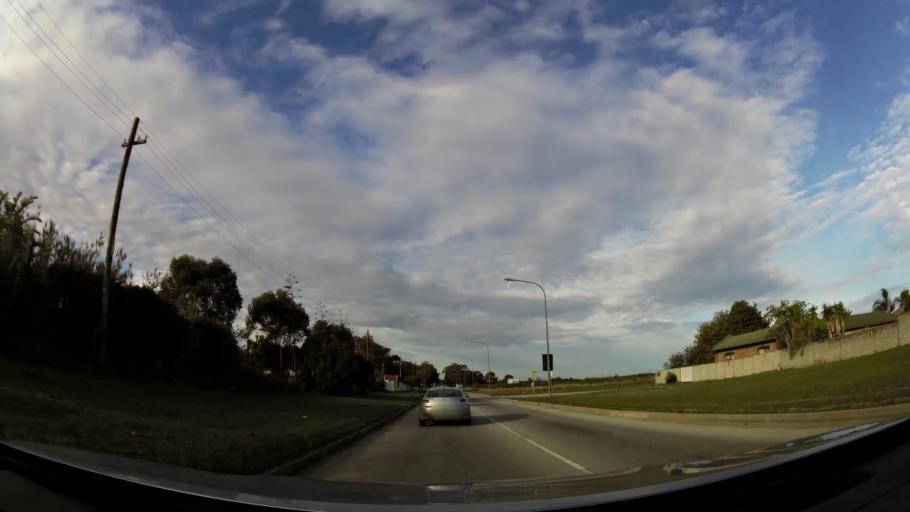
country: ZA
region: Eastern Cape
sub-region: Nelson Mandela Bay Metropolitan Municipality
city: Port Elizabeth
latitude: -33.9586
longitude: 25.4928
